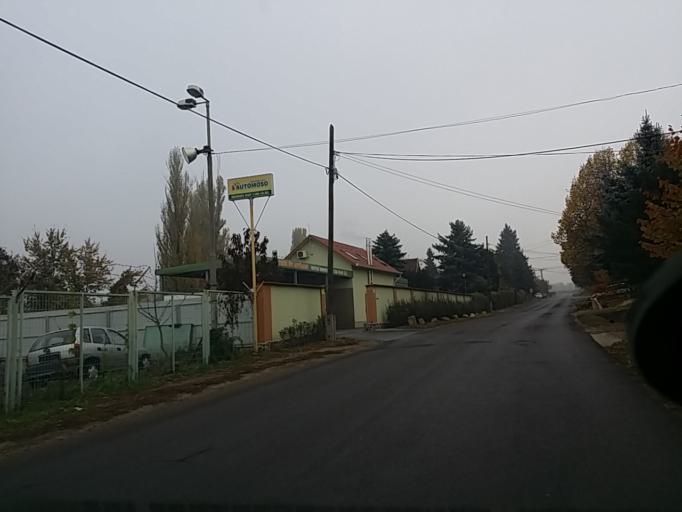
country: HU
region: Heves
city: Gyongyos
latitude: 47.7991
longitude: 19.9312
